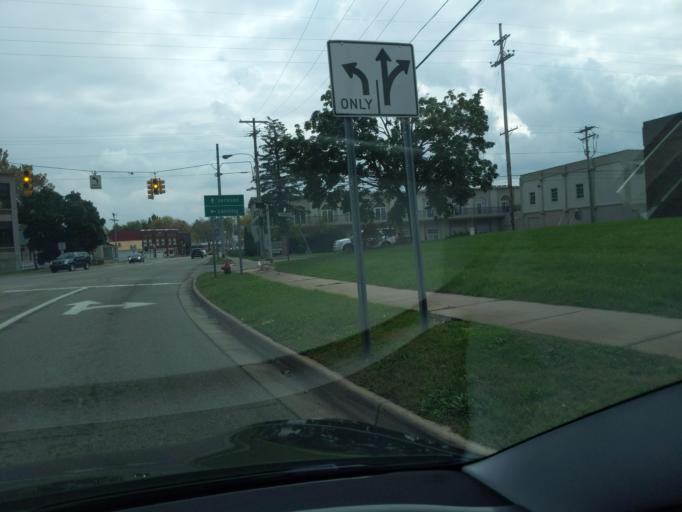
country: US
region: Michigan
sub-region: Eaton County
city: Eaton Rapids
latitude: 42.5151
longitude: -84.6568
